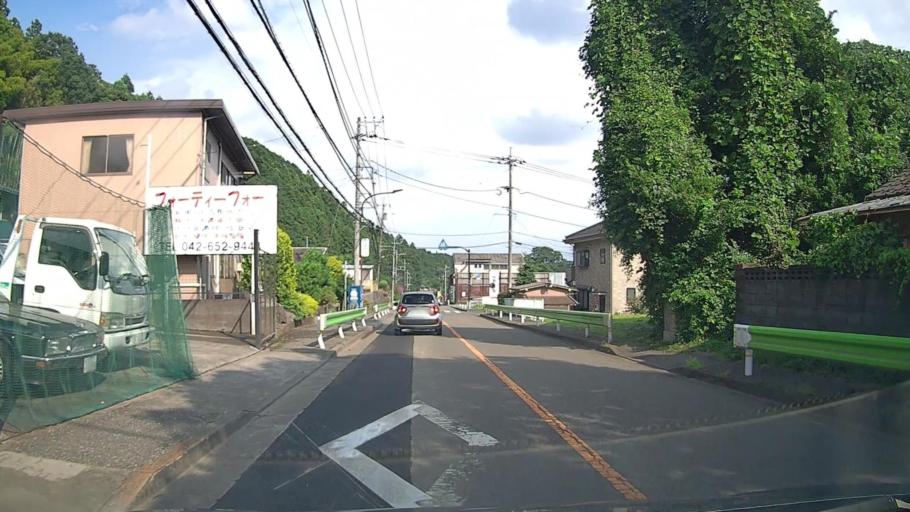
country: JP
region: Tokyo
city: Itsukaichi
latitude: 35.7108
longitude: 139.2372
